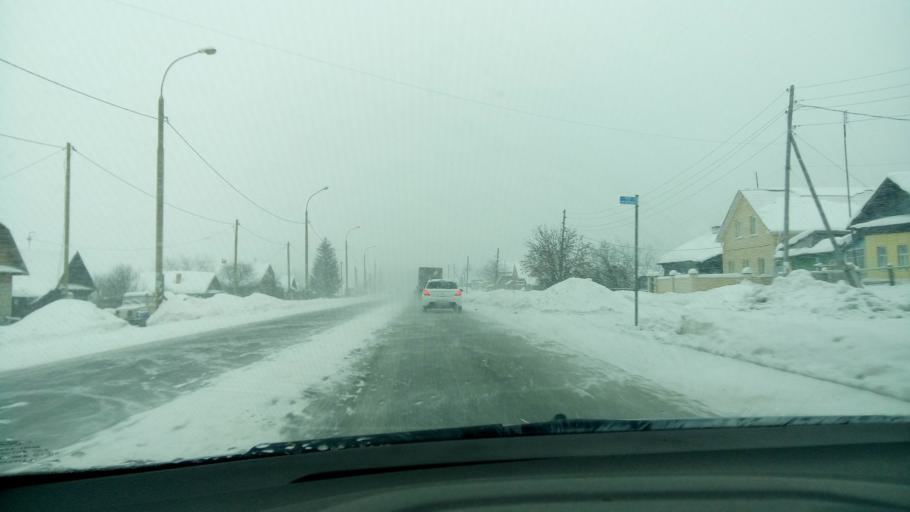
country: RU
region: Sverdlovsk
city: Beloyarskiy
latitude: 56.7706
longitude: 61.4532
